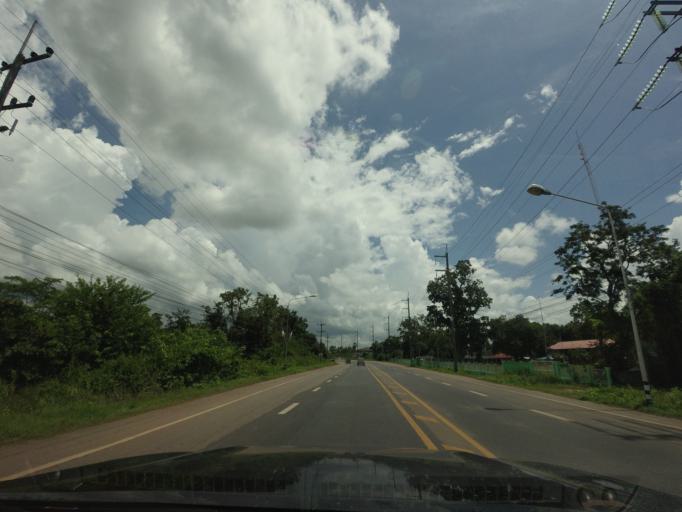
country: TH
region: Changwat Udon Thani
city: Udon Thani
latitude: 17.5338
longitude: 102.7679
